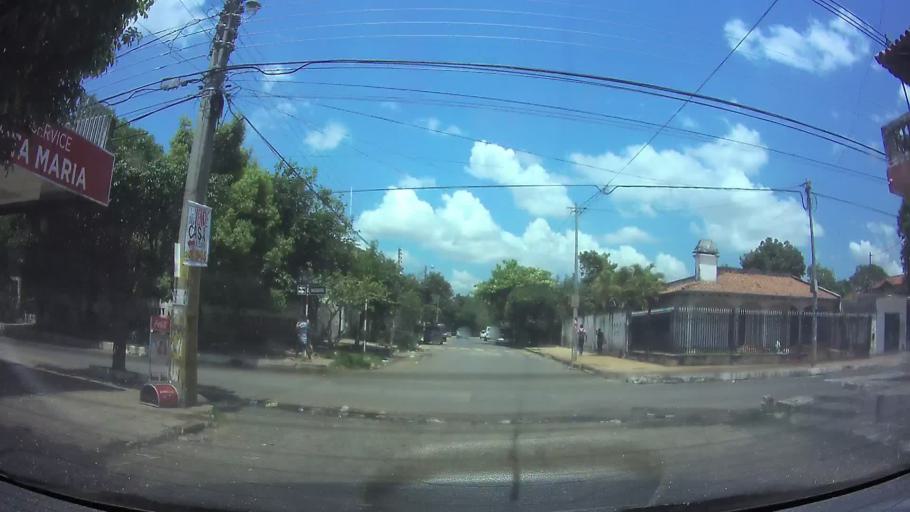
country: PY
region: Central
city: Fernando de la Mora
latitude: -25.2980
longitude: -57.5478
